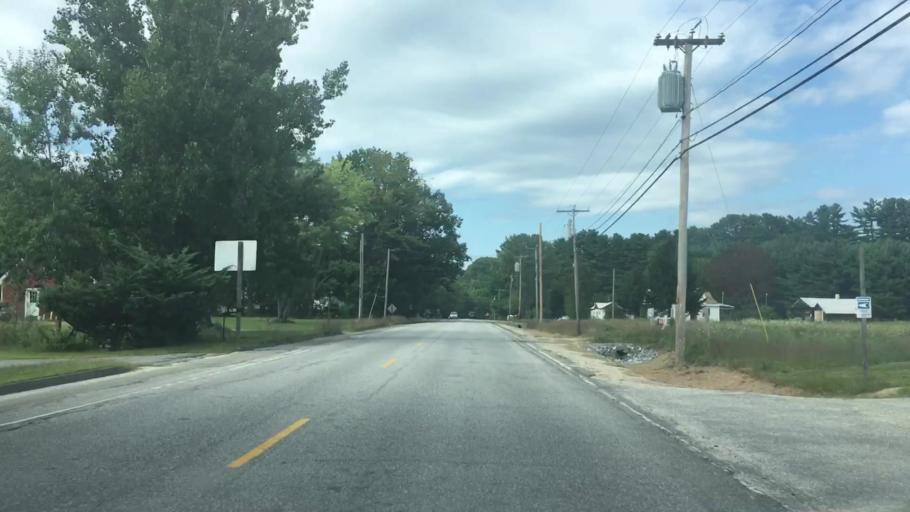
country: US
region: Maine
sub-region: Cumberland County
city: Raymond
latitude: 43.9850
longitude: -70.5187
